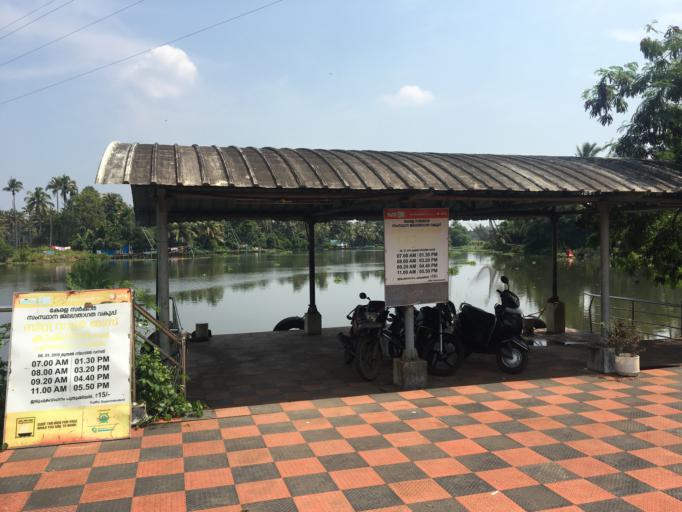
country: IN
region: Kerala
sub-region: Ernakulam
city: Cochin
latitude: 9.9675
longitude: 76.3227
